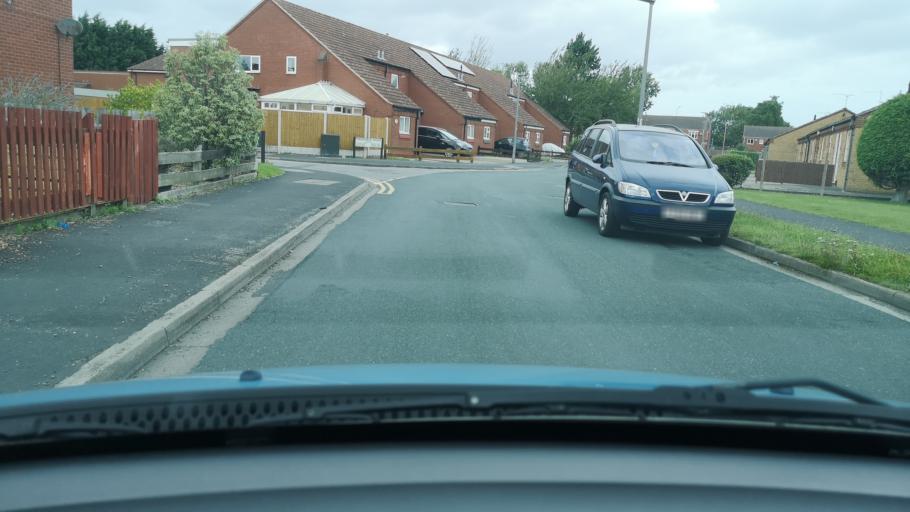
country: GB
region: England
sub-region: North Lincolnshire
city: Scunthorpe
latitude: 53.5878
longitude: -0.6888
